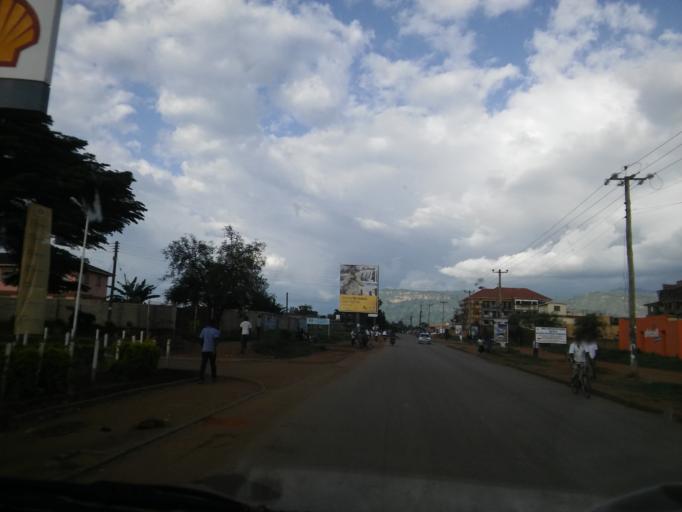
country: UG
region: Eastern Region
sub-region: Mbale District
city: Mbale
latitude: 1.0794
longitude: 34.1659
